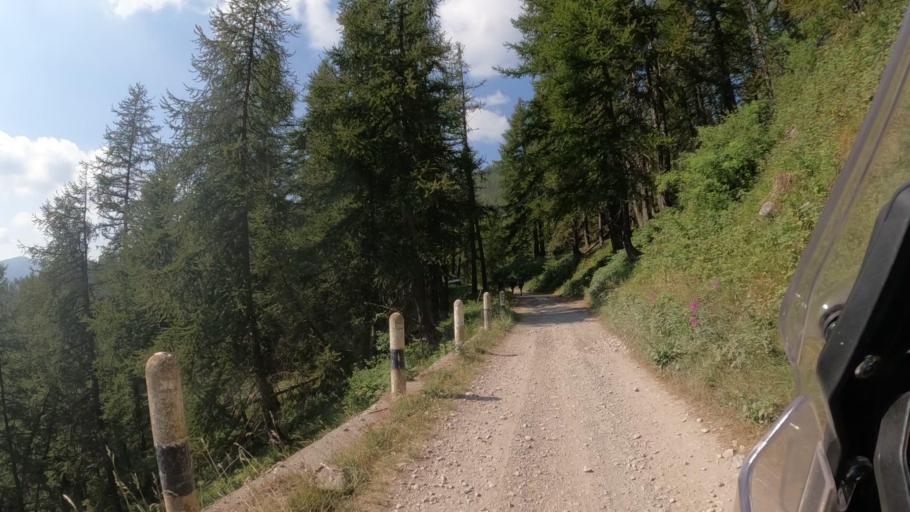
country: IT
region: Piedmont
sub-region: Provincia di Cuneo
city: Briga Alta
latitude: 44.1000
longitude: 7.7176
